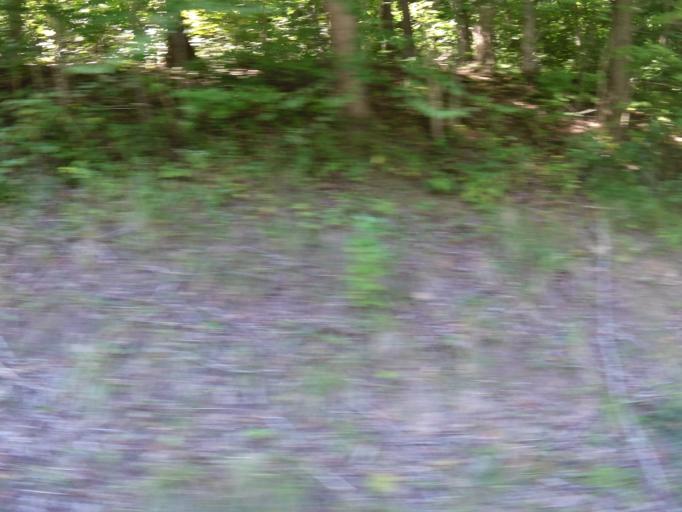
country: US
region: Kentucky
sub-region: Leslie County
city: Hyden
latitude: 37.1414
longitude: -83.4706
